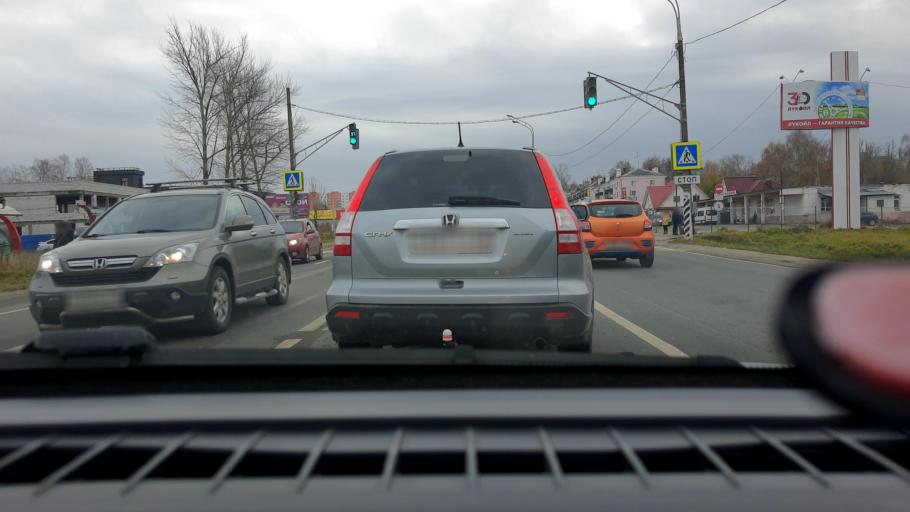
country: RU
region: Nizjnij Novgorod
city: Kstovo
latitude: 56.1582
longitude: 44.1960
